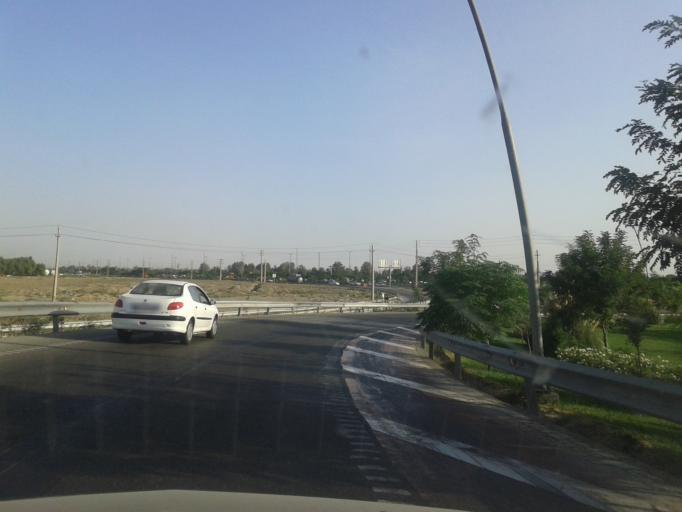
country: IR
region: Tehran
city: Eslamshahr
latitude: 35.6509
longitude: 51.2764
